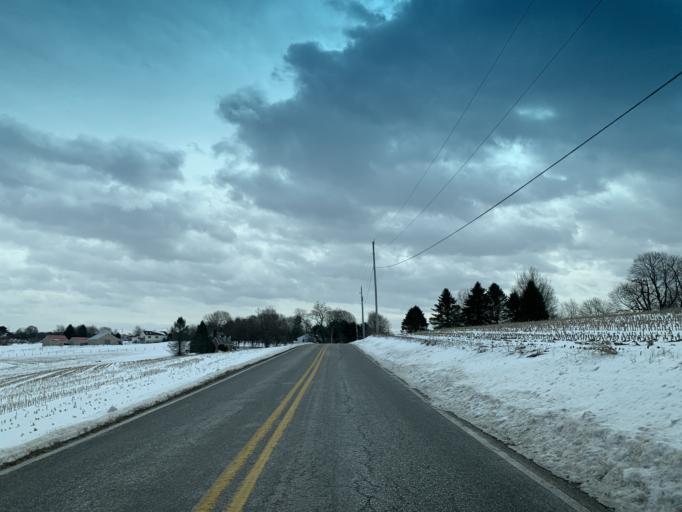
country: US
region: Pennsylvania
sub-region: York County
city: Shrewsbury
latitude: 39.7872
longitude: -76.6458
